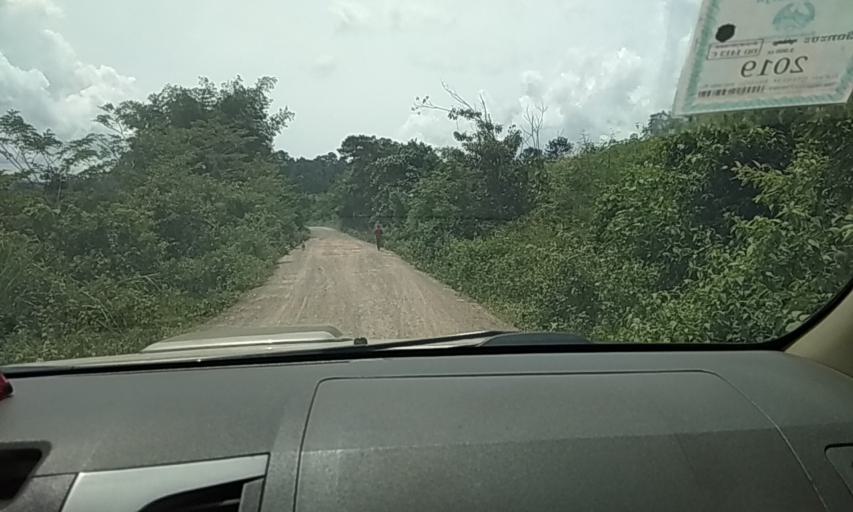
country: LA
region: Bolikhamxai
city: Ban Nahin
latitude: 18.1497
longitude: 104.7351
